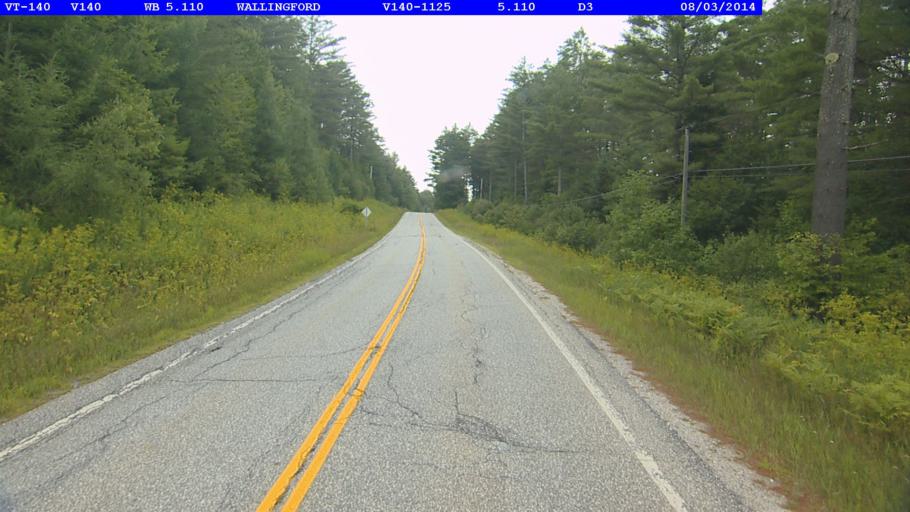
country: US
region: Vermont
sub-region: Rutland County
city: Rutland
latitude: 43.4594
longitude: -72.8893
